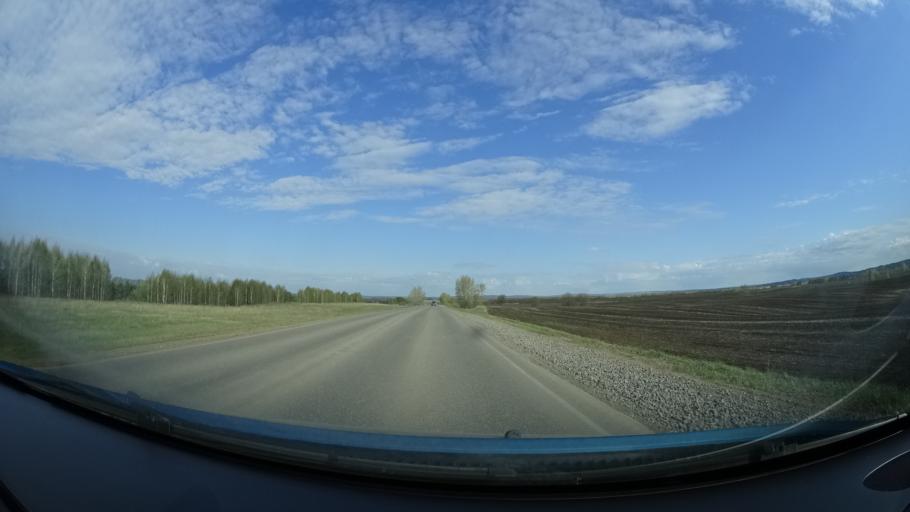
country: RU
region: Bashkortostan
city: Blagoveshchensk
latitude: 55.1899
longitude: 55.8416
